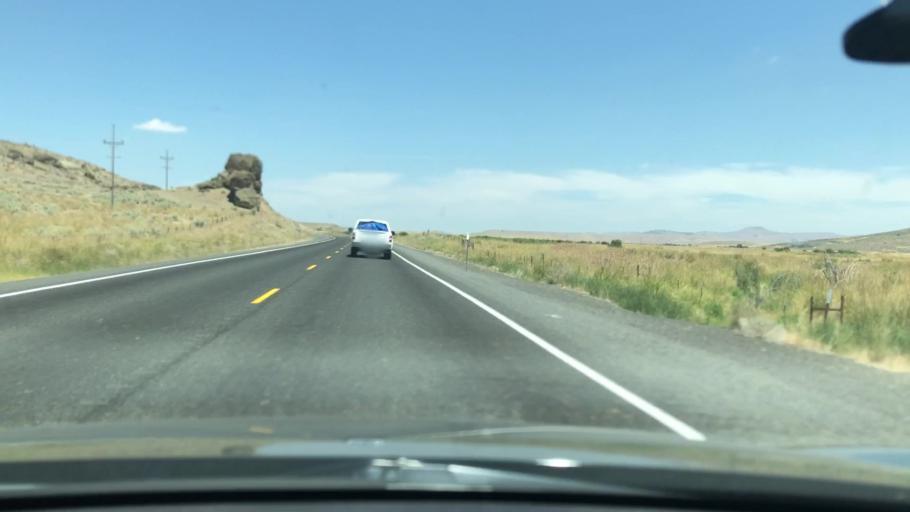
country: US
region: Idaho
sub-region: Owyhee County
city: Marsing
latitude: 43.1101
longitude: -117.0564
